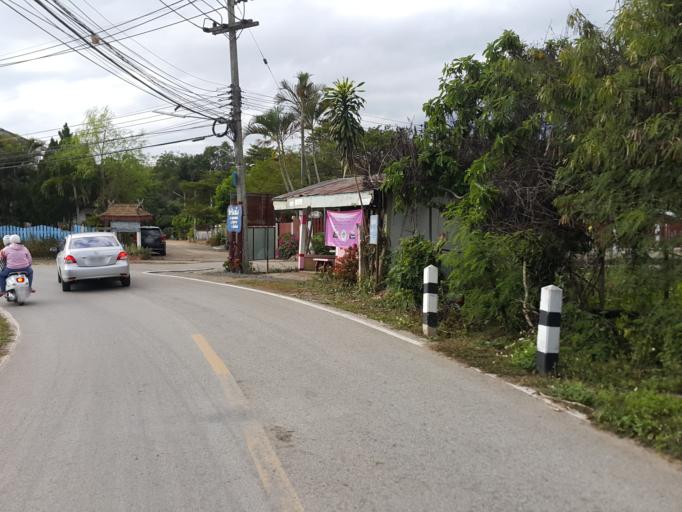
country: TH
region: Chiang Mai
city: San Sai
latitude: 18.8820
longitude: 99.1016
